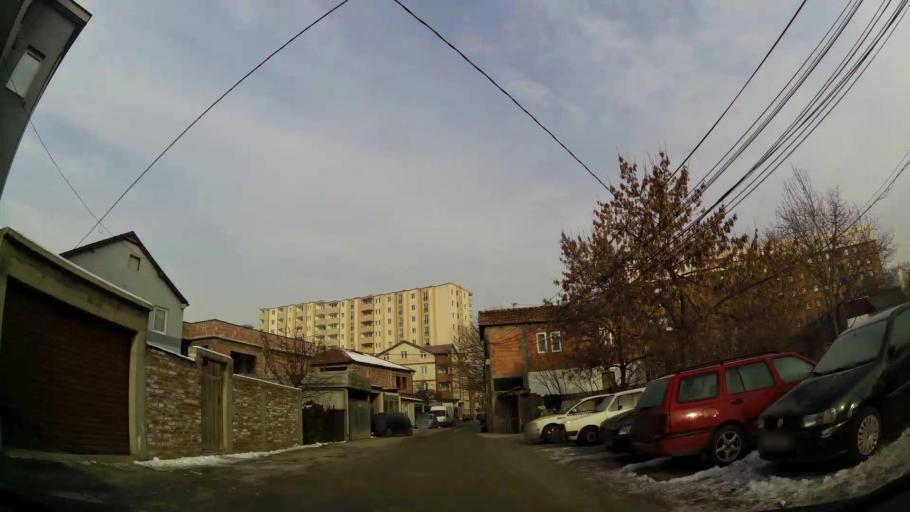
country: MK
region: Cair
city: Cair
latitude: 42.0208
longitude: 21.4385
